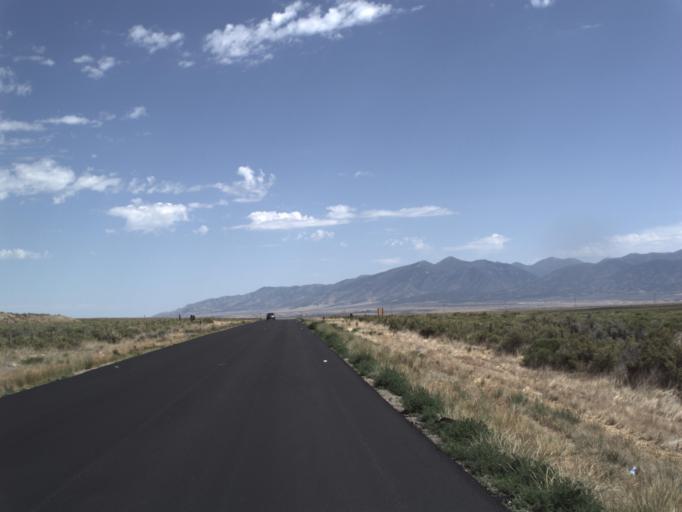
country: US
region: Utah
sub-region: Tooele County
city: Tooele
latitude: 40.1978
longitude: -112.4134
